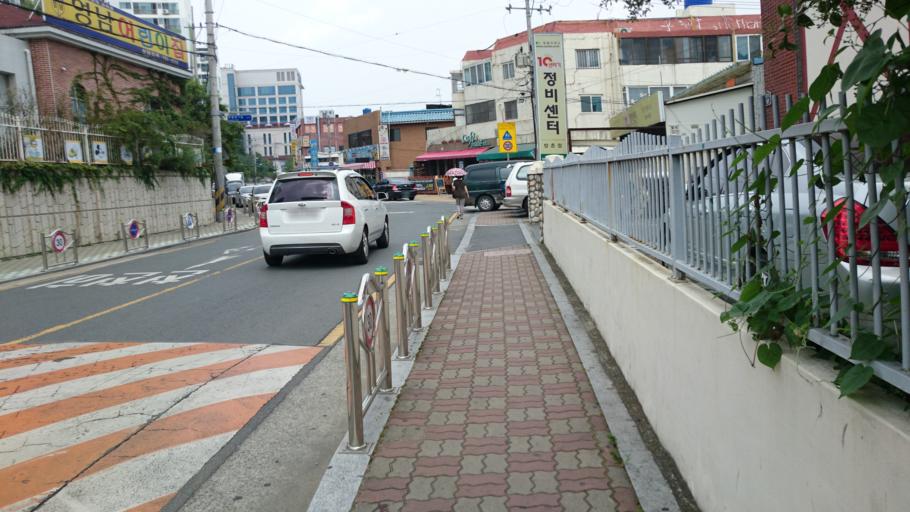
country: KR
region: Daegu
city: Daegu
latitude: 35.8799
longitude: 128.6612
